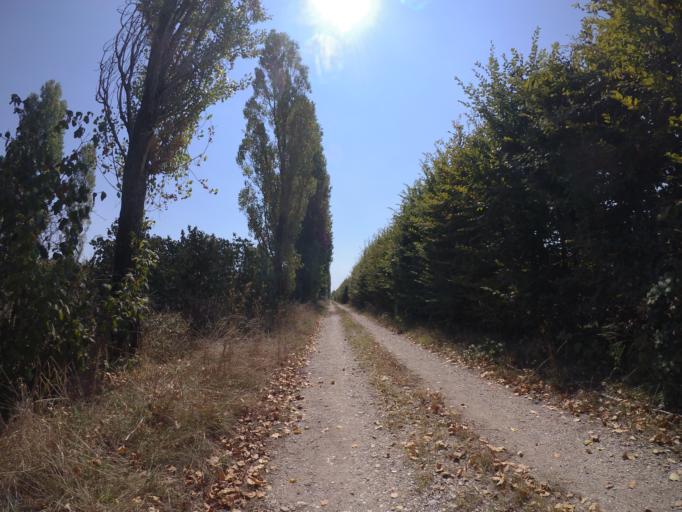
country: IT
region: Friuli Venezia Giulia
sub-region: Provincia di Udine
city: Codroipo
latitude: 45.9656
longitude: 13.0108
